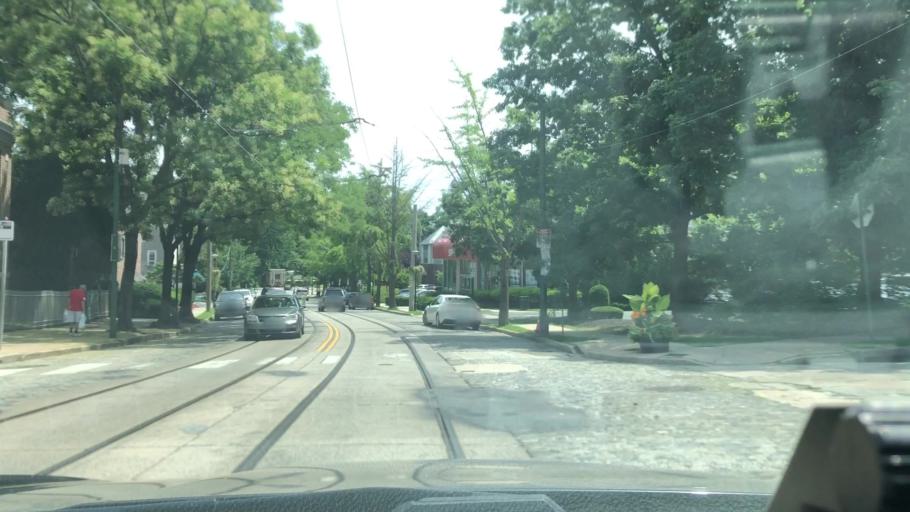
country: US
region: Pennsylvania
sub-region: Montgomery County
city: Wyndmoor
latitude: 40.0688
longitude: -75.1990
